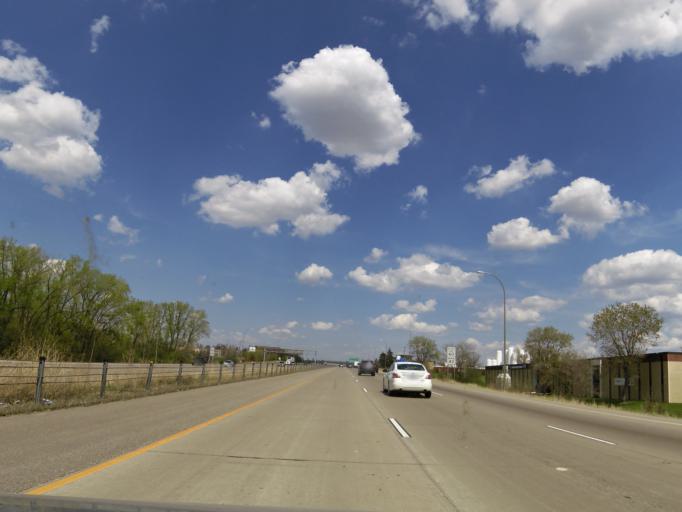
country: US
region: Minnesota
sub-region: Washington County
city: Woodbury
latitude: 44.9187
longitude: -92.9763
